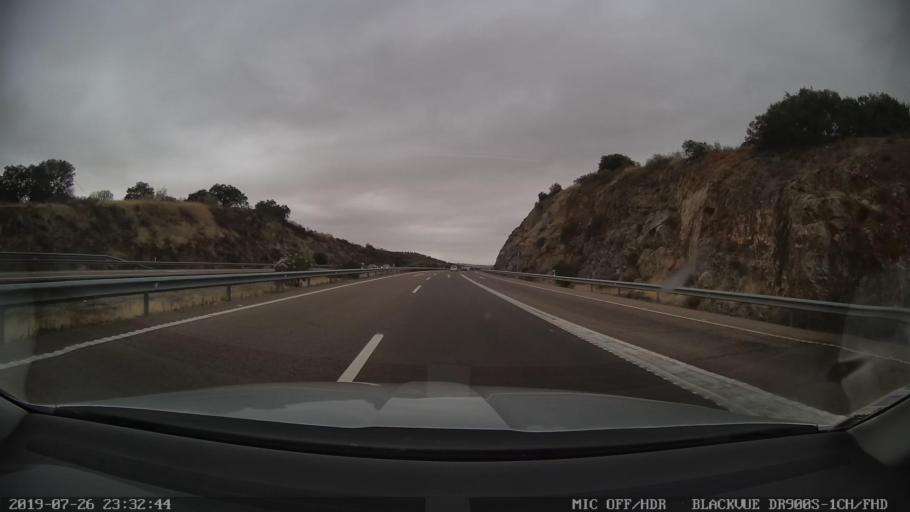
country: ES
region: Extremadura
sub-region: Provincia de Caceres
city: Puerto de Santa Cruz
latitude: 39.3254
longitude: -5.8580
